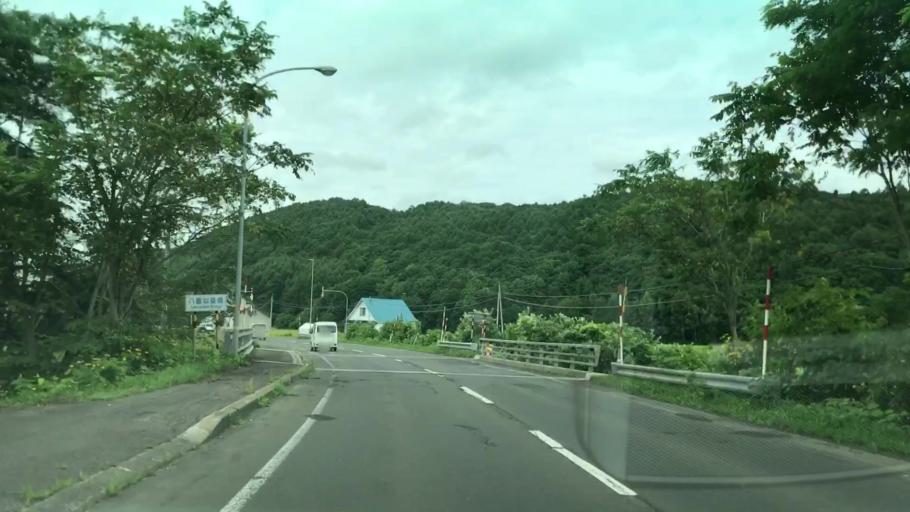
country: JP
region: Hokkaido
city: Iwanai
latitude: 42.9644
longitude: 140.6920
